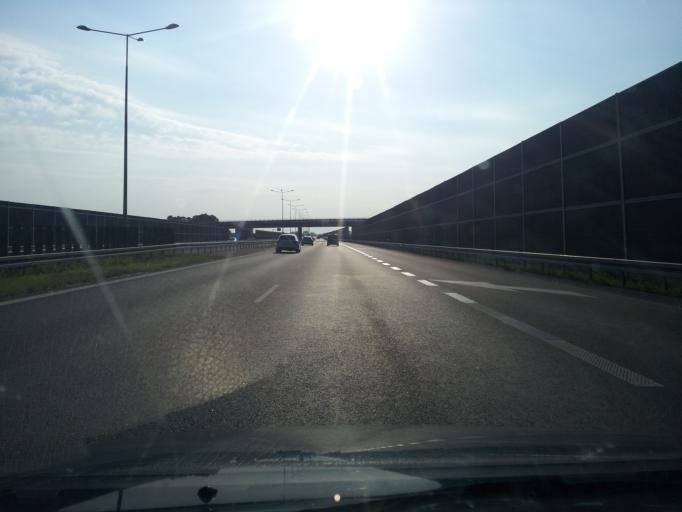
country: PL
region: Masovian Voivodeship
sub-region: Powiat zyrardowski
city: Zyrardow
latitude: 52.1095
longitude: 20.4577
